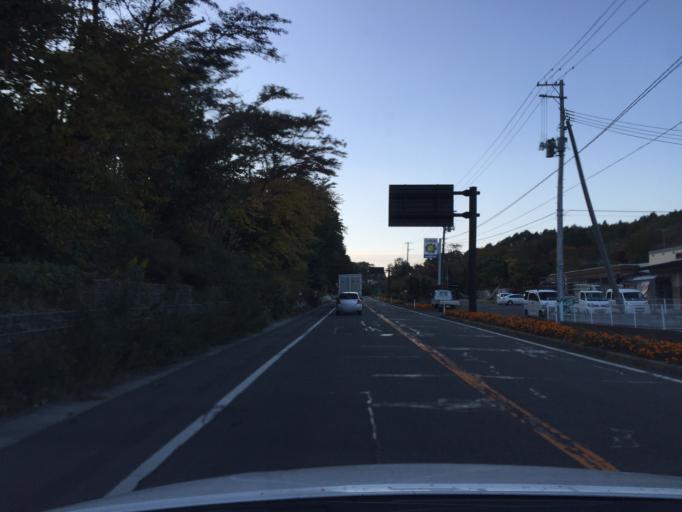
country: JP
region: Fukushima
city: Ishikawa
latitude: 37.2694
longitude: 140.5519
